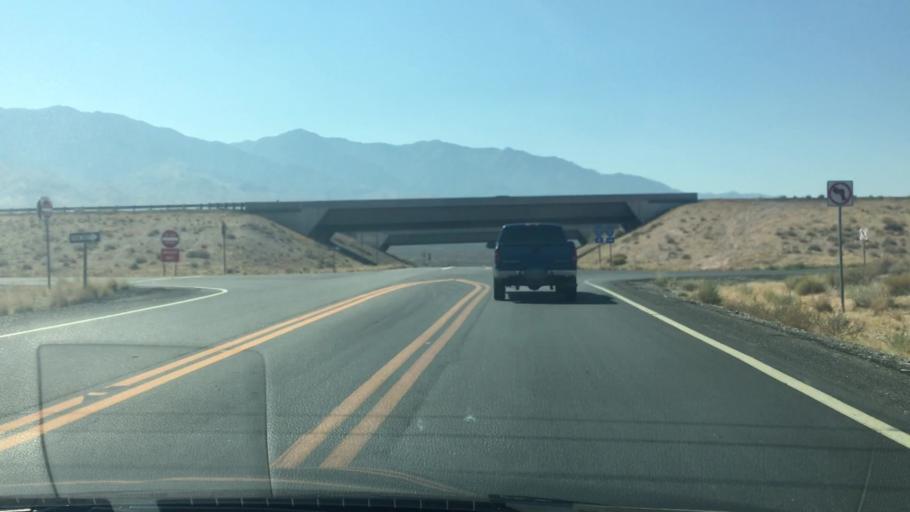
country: US
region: Arizona
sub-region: Mohave County
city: Beaver Dam
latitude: 36.8929
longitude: -113.9301
